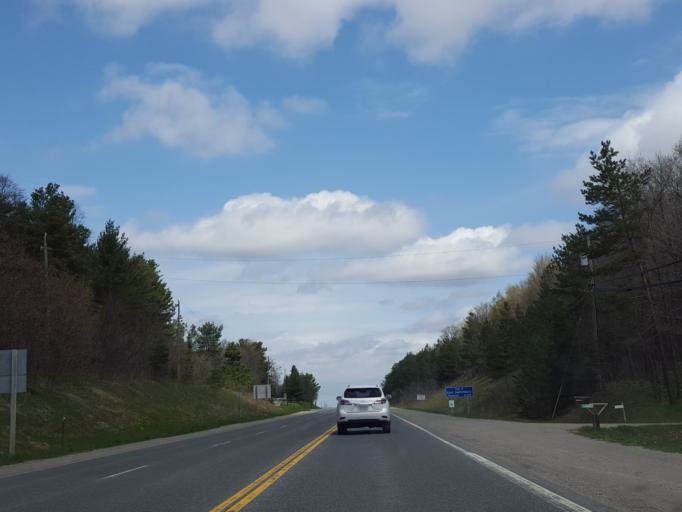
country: CA
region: Ontario
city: Newmarket
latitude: 44.0963
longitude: -79.3107
